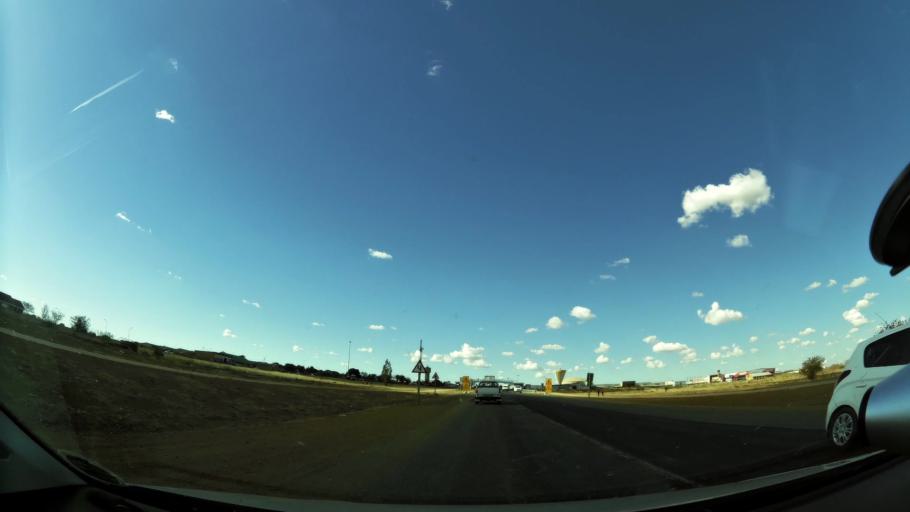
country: ZA
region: North-West
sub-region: Dr Kenneth Kaunda District Municipality
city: Klerksdorp
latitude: -26.8769
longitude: 26.5873
